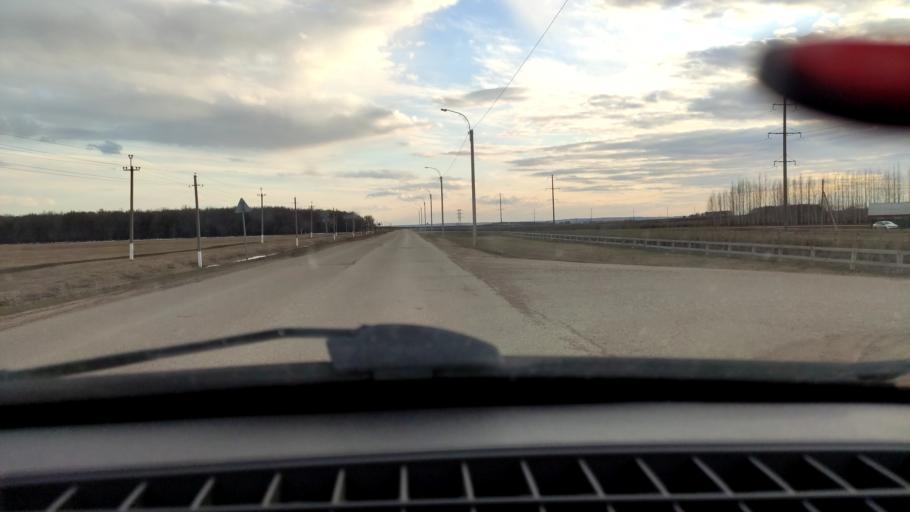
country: RU
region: Bashkortostan
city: Tolbazy
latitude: 54.0011
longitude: 55.8577
